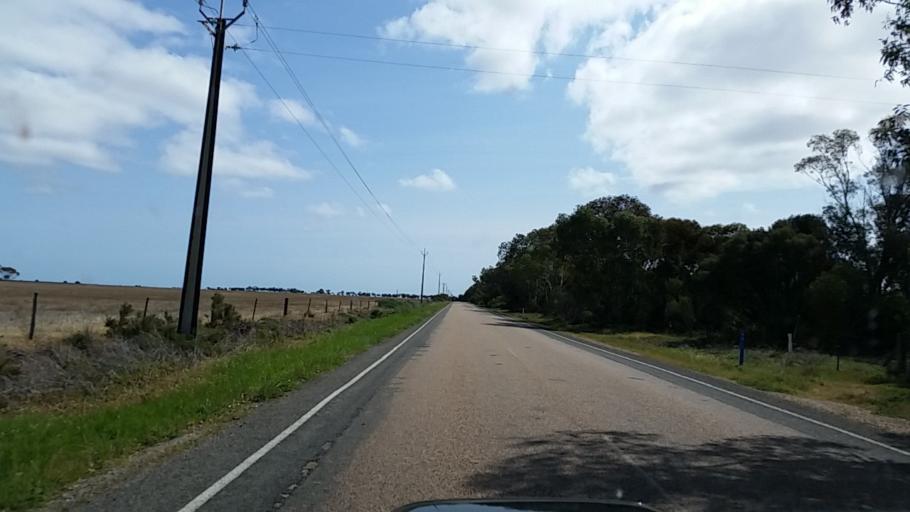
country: AU
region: South Australia
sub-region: Port Pirie City and Dists
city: Solomontown
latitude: -33.2301
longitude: 138.0214
